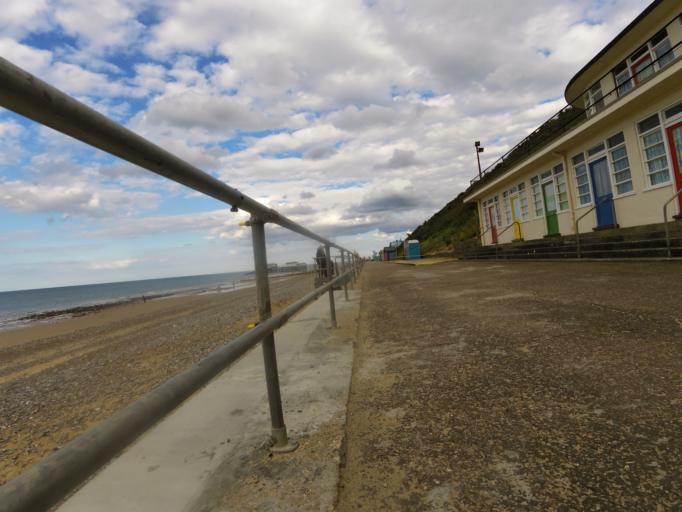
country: GB
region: England
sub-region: Norfolk
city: Cromer
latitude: 52.9340
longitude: 1.2925
